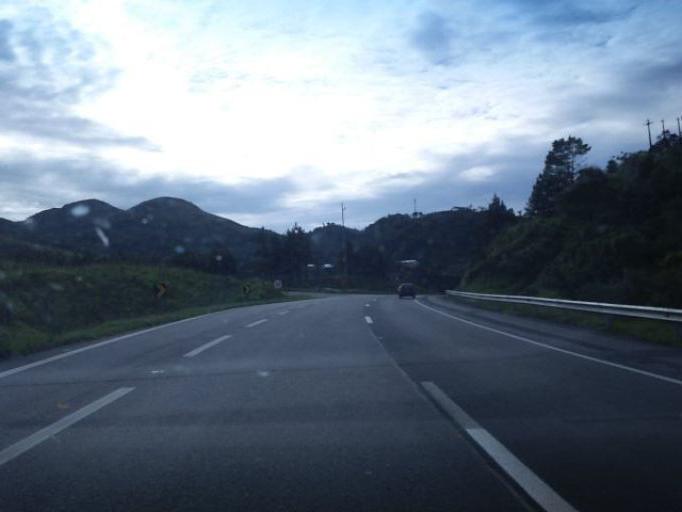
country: BR
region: Parana
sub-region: Campina Grande Do Sul
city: Campina Grande do Sul
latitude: -25.1091
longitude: -48.7998
